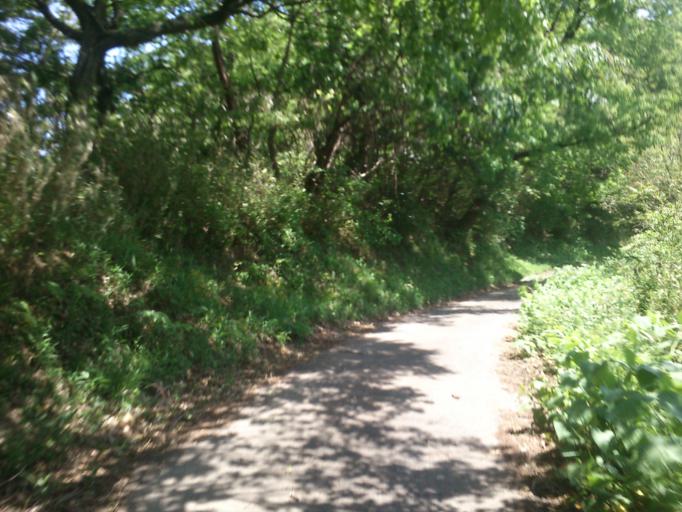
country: JP
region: Kyoto
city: Miyazu
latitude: 35.7167
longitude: 135.1364
